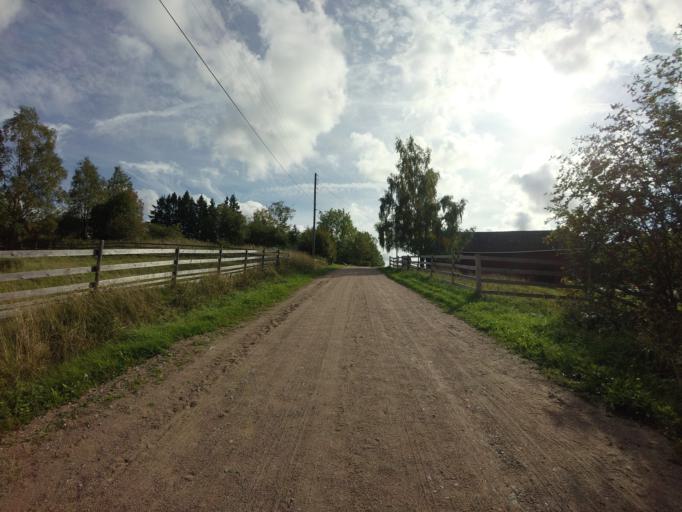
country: FI
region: Varsinais-Suomi
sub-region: Turku
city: Kaarina
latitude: 60.4630
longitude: 22.3349
